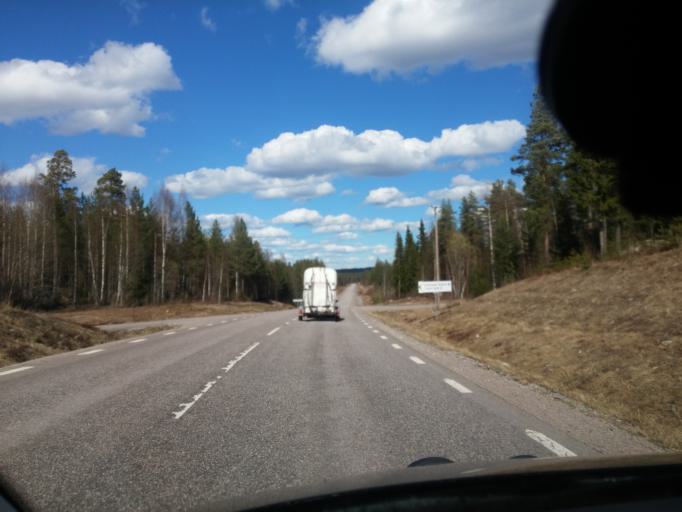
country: SE
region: Gaevleborg
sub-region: Ovanakers Kommun
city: Edsbyn
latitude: 61.2578
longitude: 15.8841
